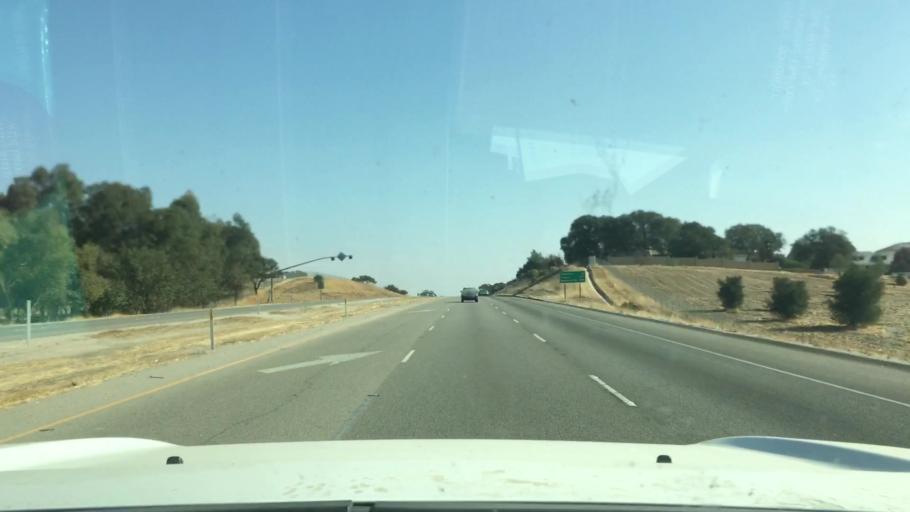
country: US
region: California
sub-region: San Luis Obispo County
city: Paso Robles
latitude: 35.6446
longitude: -120.6695
